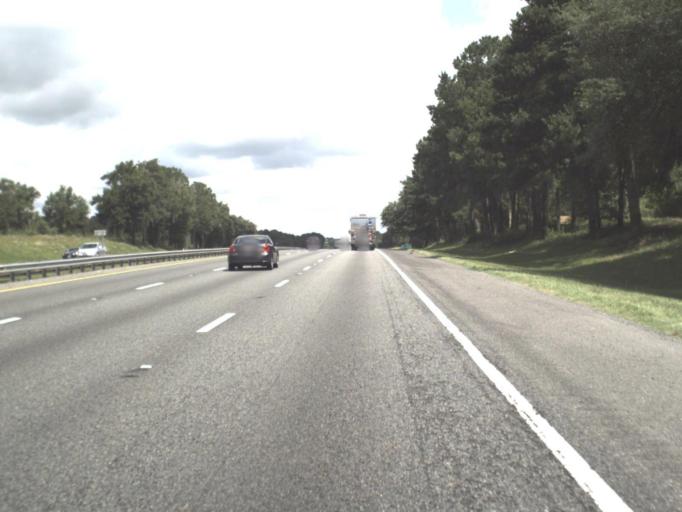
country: US
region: Florida
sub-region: Columbia County
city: Lake City
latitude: 30.1878
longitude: -82.6925
